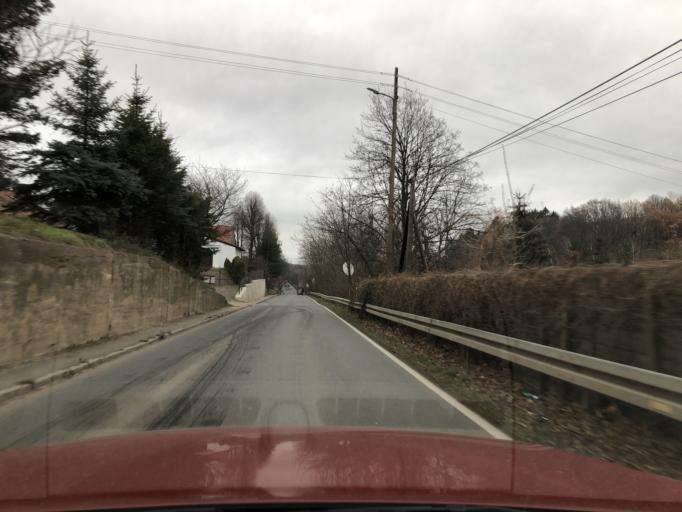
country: PL
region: Lower Silesian Voivodeship
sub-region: Powiat walbrzyski
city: Stare Bogaczowice
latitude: 50.8056
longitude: 16.2071
